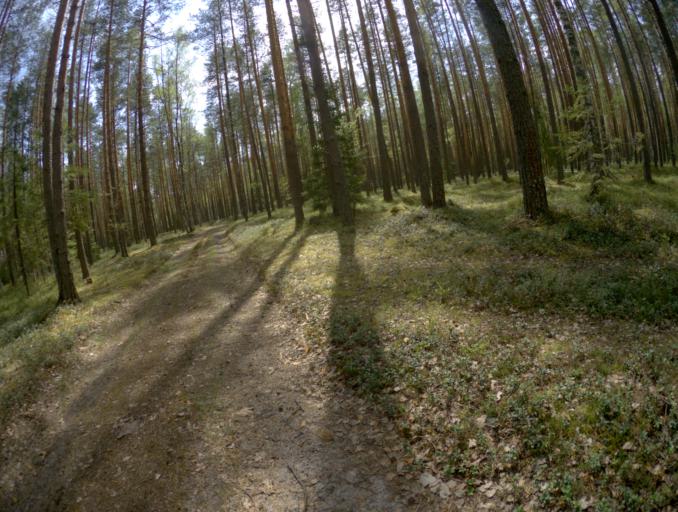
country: RU
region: Vladimir
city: Golovino
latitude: 55.9254
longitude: 40.3858
